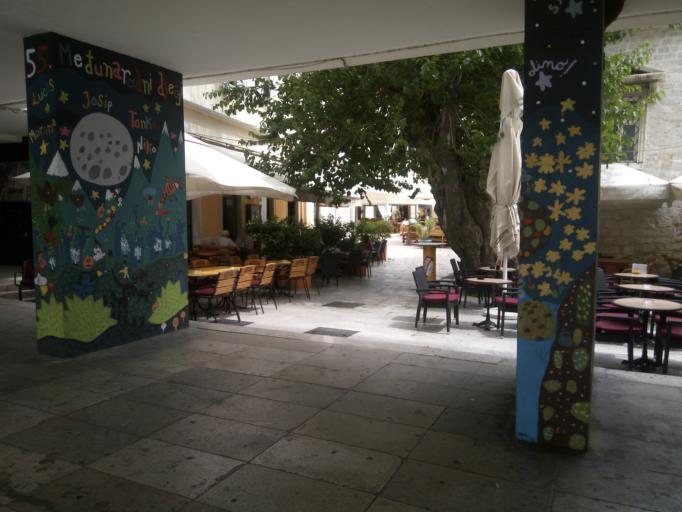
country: HR
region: Sibensko-Kniniska
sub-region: Grad Sibenik
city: Sibenik
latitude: 43.7345
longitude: 15.8902
